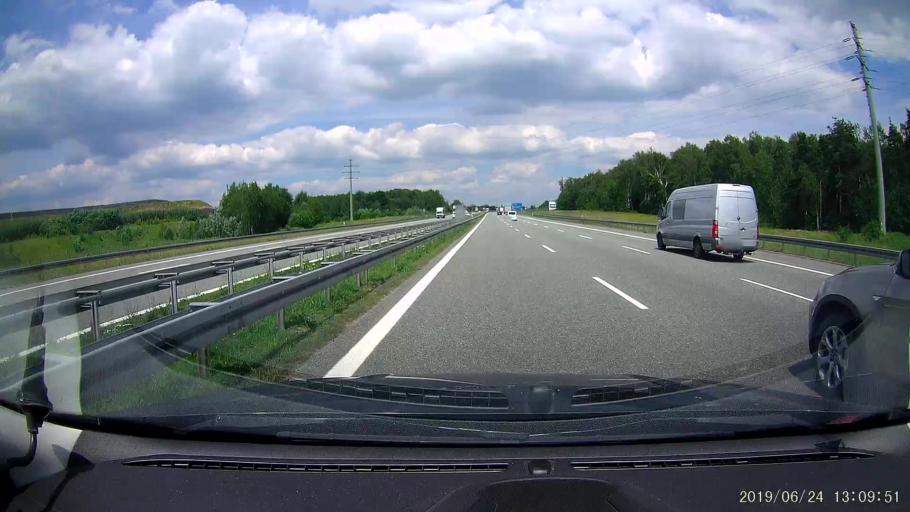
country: PL
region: Silesian Voivodeship
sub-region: Powiat gliwicki
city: Gieraltowice
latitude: 50.2065
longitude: 18.6965
